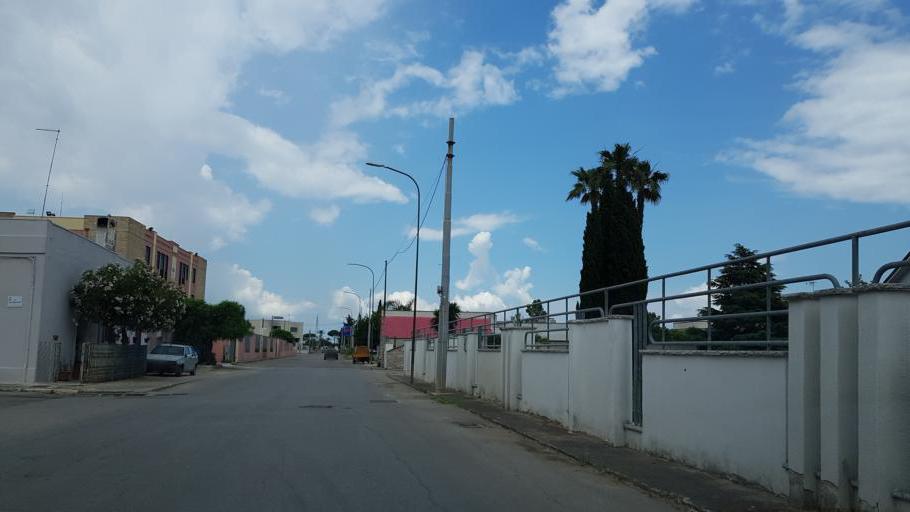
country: IT
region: Apulia
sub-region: Provincia di Brindisi
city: San Donaci
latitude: 40.4541
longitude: 17.9206
